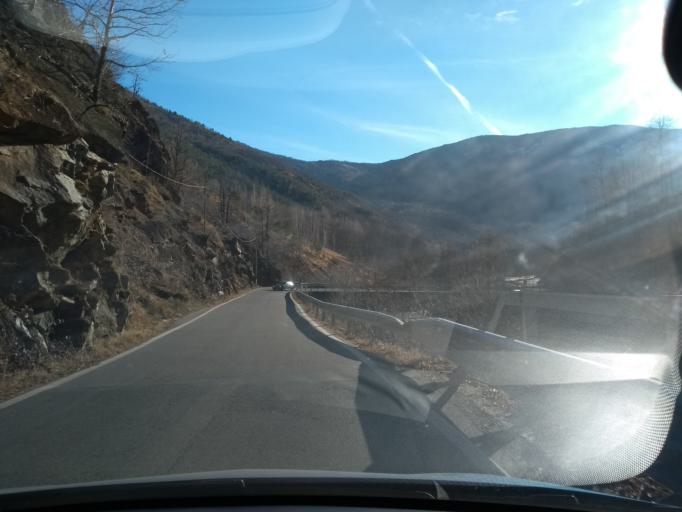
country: IT
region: Piedmont
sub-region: Provincia di Torino
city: La Villa
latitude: 45.2451
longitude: 7.4327
